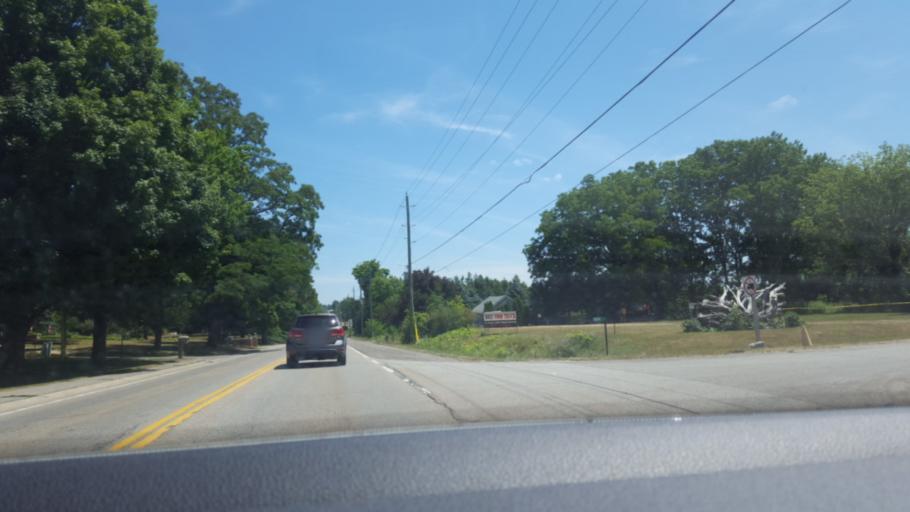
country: CA
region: Ontario
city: Ancaster
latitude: 43.1973
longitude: -80.0085
